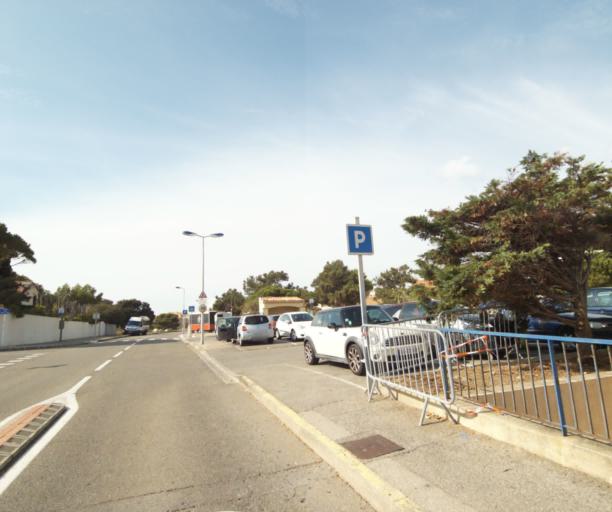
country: FR
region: Provence-Alpes-Cote d'Azur
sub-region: Departement des Bouches-du-Rhone
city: Sausset-les-Pins
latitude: 43.3310
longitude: 5.0985
